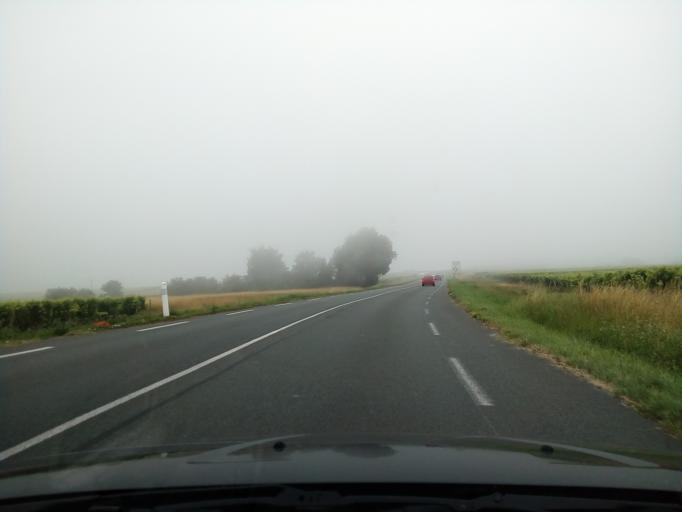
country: FR
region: Poitou-Charentes
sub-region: Departement de la Charente-Maritime
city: Cherac
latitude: 45.6905
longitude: -0.4071
